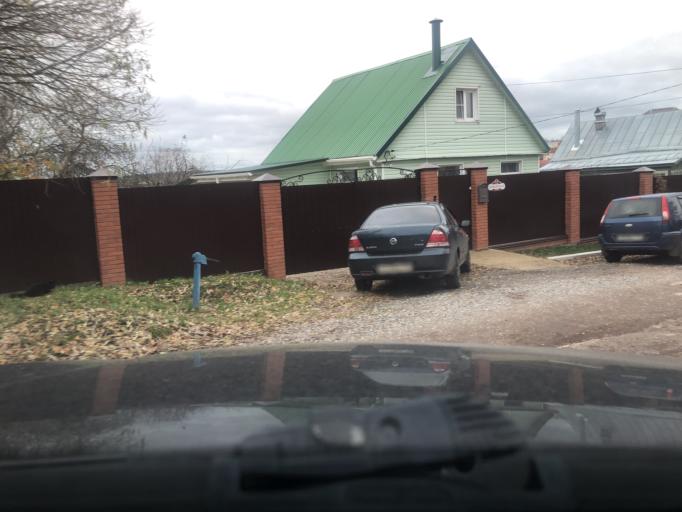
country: RU
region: Moskovskaya
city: Sergiyev Posad
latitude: 56.3004
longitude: 38.1193
